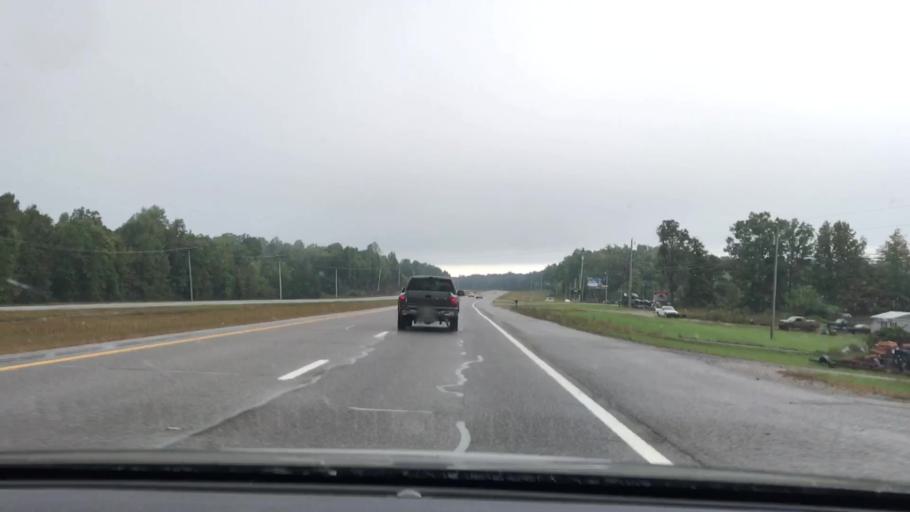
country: US
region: Tennessee
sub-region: Fentress County
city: Jamestown
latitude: 36.3608
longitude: -84.9476
